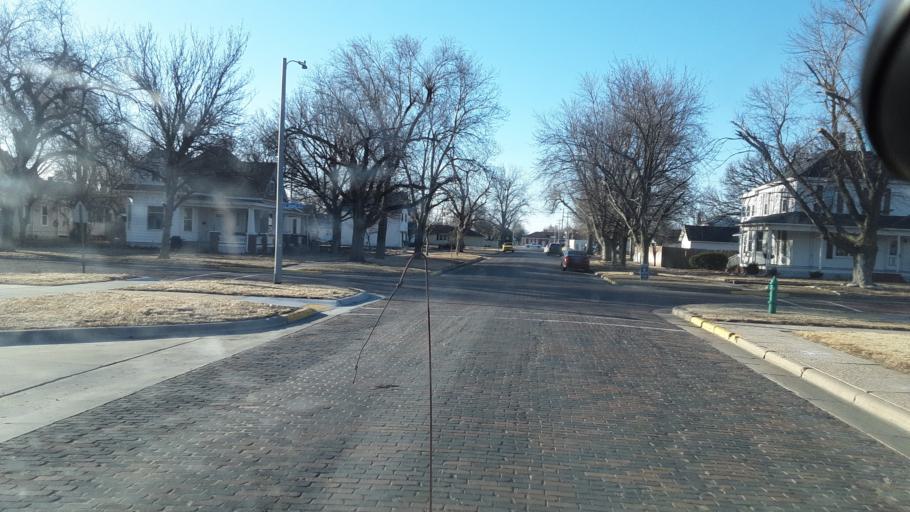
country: US
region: Kansas
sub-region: Barton County
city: Ellinwood
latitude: 38.3560
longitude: -98.5793
